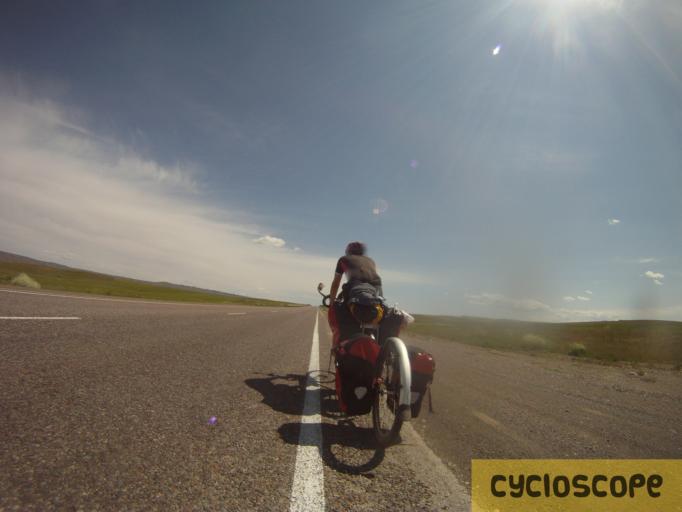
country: KZ
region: Zhambyl
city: Georgiyevka
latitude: 43.2942
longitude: 74.8759
